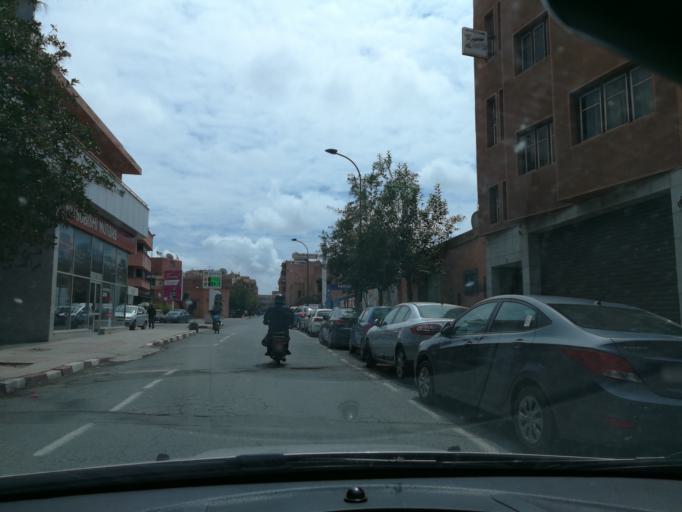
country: MA
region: Marrakech-Tensift-Al Haouz
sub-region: Marrakech
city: Marrakesh
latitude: 31.6342
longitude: -8.0146
